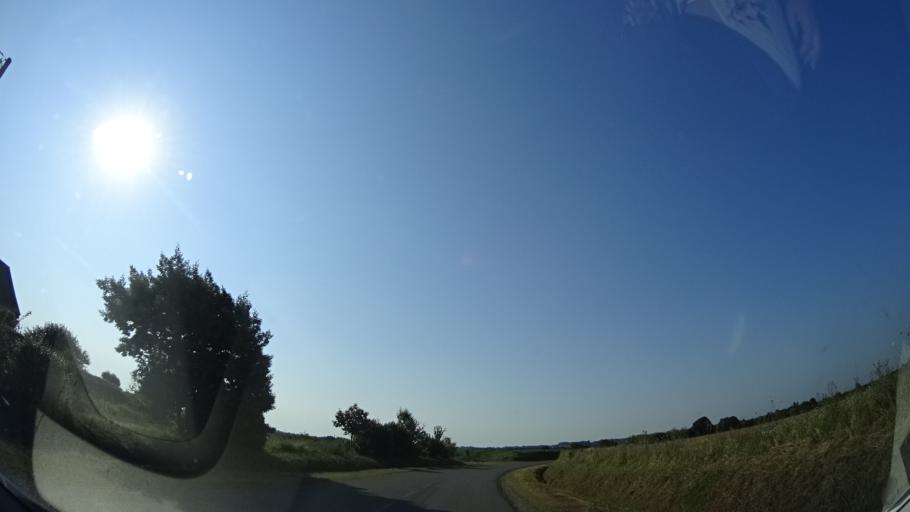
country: FR
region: Brittany
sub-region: Departement d'Ille-et-Vilaine
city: Pace
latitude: 48.1672
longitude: -1.7868
